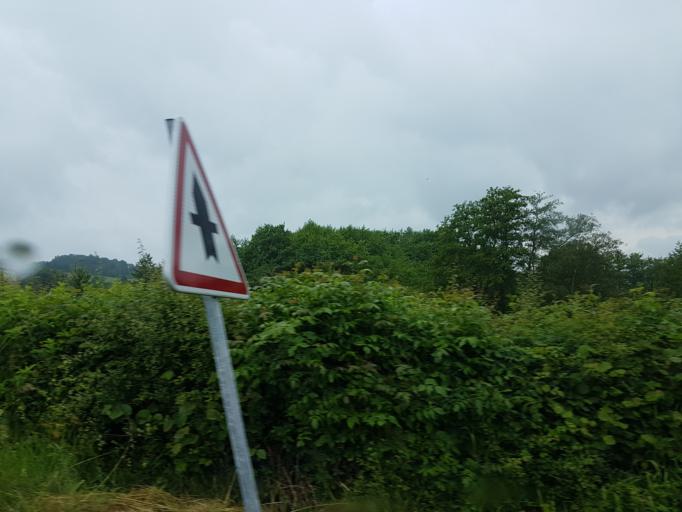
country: FR
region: Bourgogne
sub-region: Departement de la Nievre
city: Chateau-Chinon(Ville)
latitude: 47.1620
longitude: 3.8549
